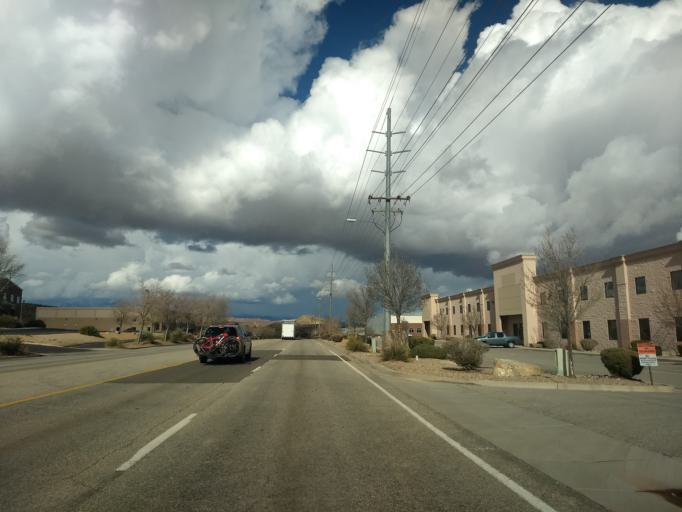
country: US
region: Utah
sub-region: Washington County
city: Saint George
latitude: 37.0369
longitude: -113.5590
